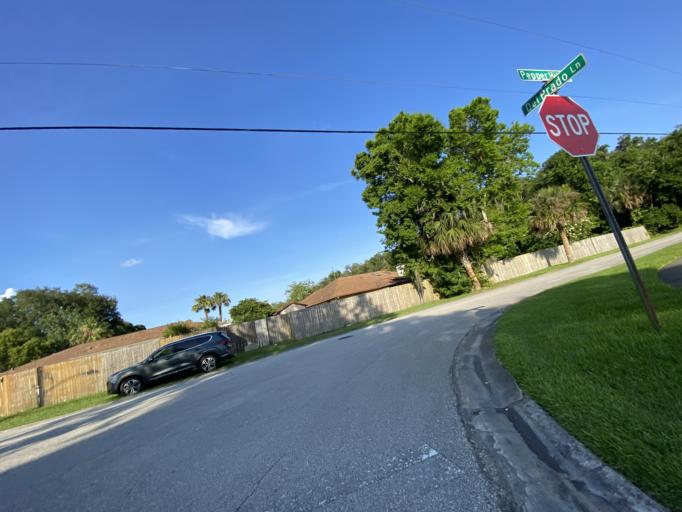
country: US
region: Florida
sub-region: Volusia County
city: South Daytona
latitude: 29.1490
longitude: -81.0099
